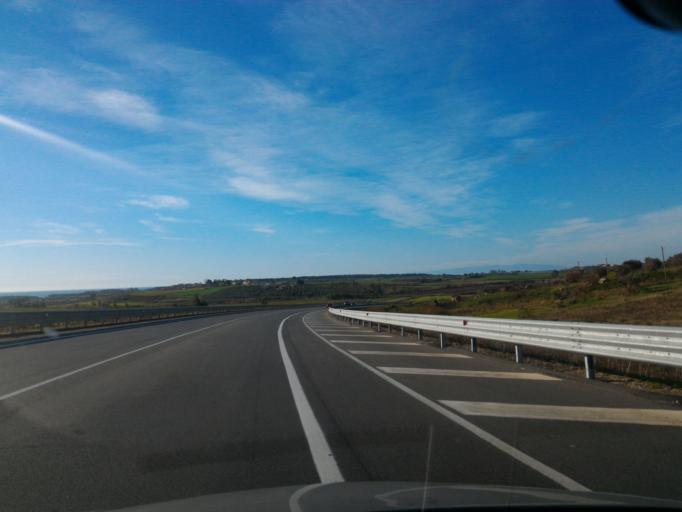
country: IT
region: Calabria
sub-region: Provincia di Crotone
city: Isola di Capo Rizzuto
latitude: 38.9424
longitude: 17.0802
